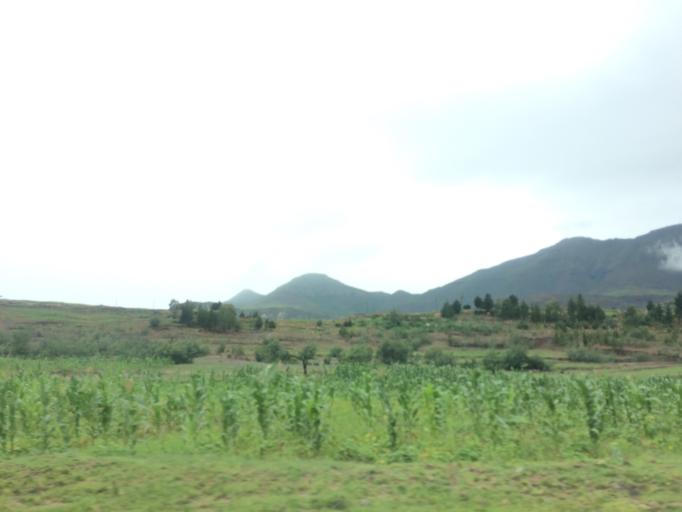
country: LS
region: Mafeteng
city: Mafeteng
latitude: -29.7814
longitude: 27.5217
